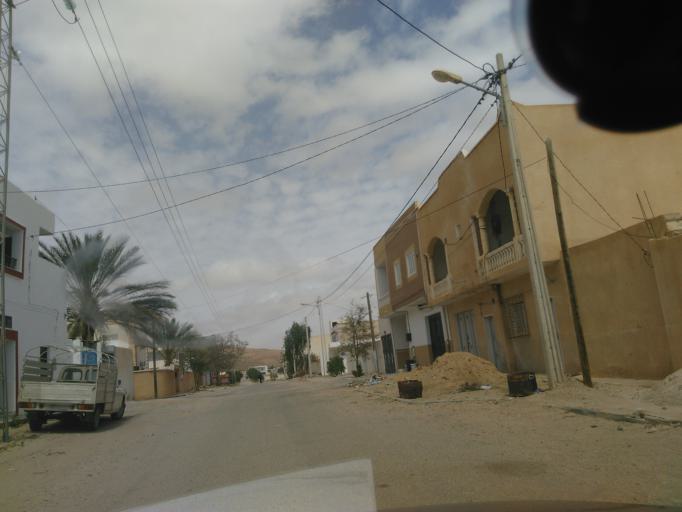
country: TN
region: Tataouine
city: Tataouine
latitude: 32.9505
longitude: 10.4651
